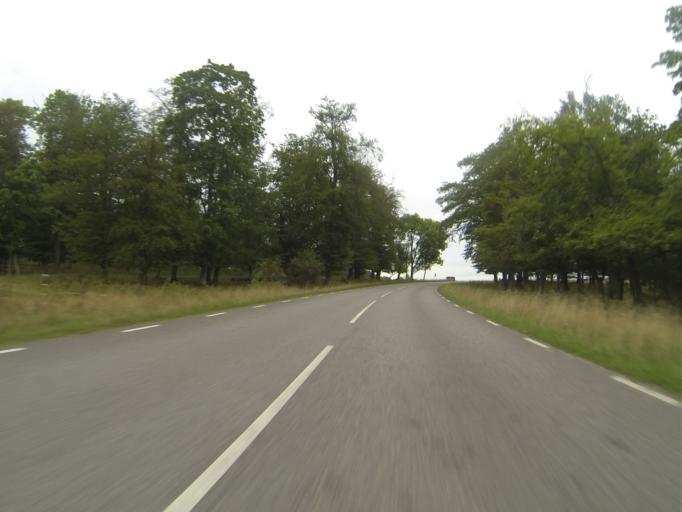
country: SE
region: Skane
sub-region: Lunds Kommun
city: Veberod
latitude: 55.6935
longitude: 13.4209
